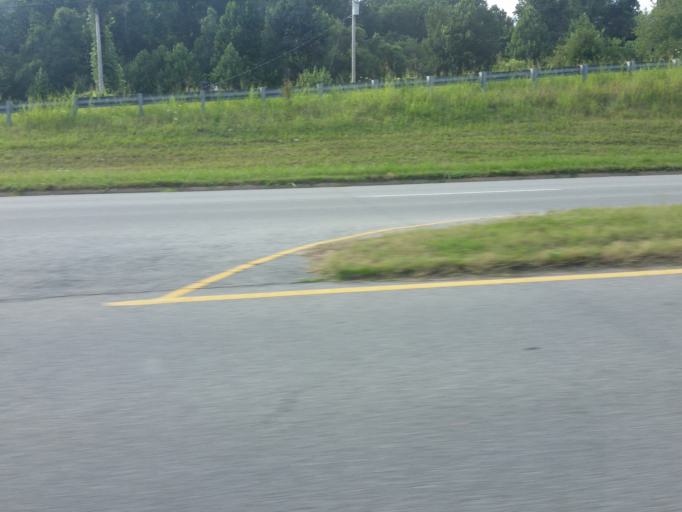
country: US
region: Tennessee
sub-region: Humphreys County
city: New Johnsonville
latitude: 36.0227
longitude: -87.9631
